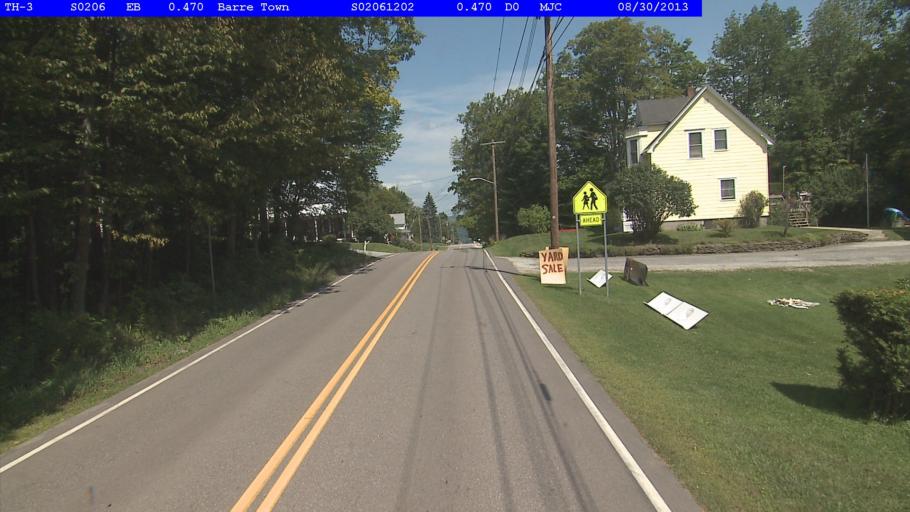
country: US
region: Vermont
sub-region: Washington County
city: South Barre
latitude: 44.1517
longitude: -72.4755
